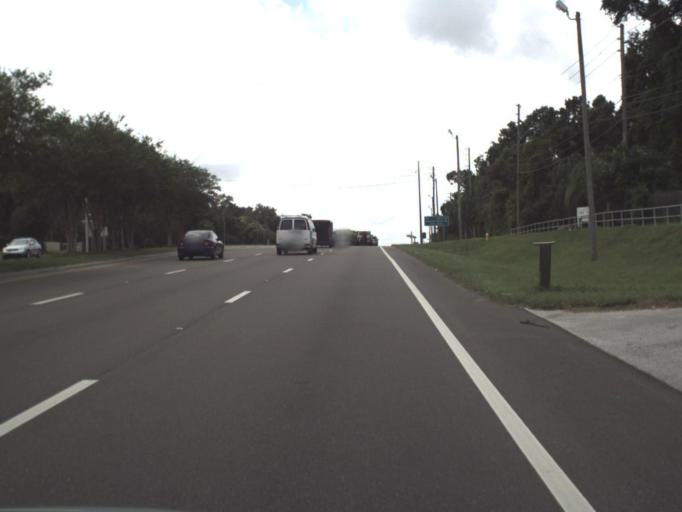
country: US
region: Florida
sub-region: Pinellas County
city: Safety Harbor
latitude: 27.9951
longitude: -82.7090
